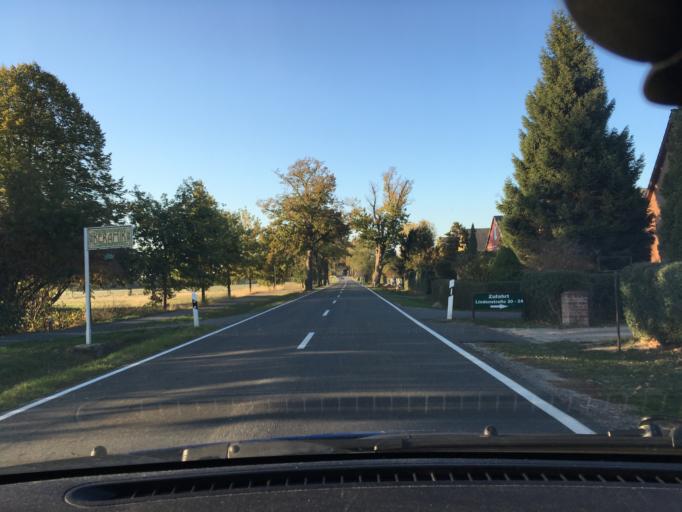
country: DE
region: Lower Saxony
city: Bleckede
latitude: 53.3338
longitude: 10.8016
